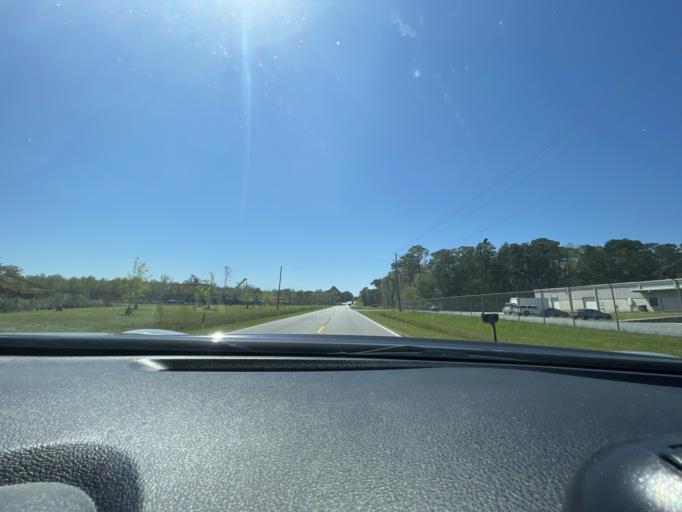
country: US
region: Georgia
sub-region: Chatham County
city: Pooler
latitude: 32.0983
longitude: -81.2296
